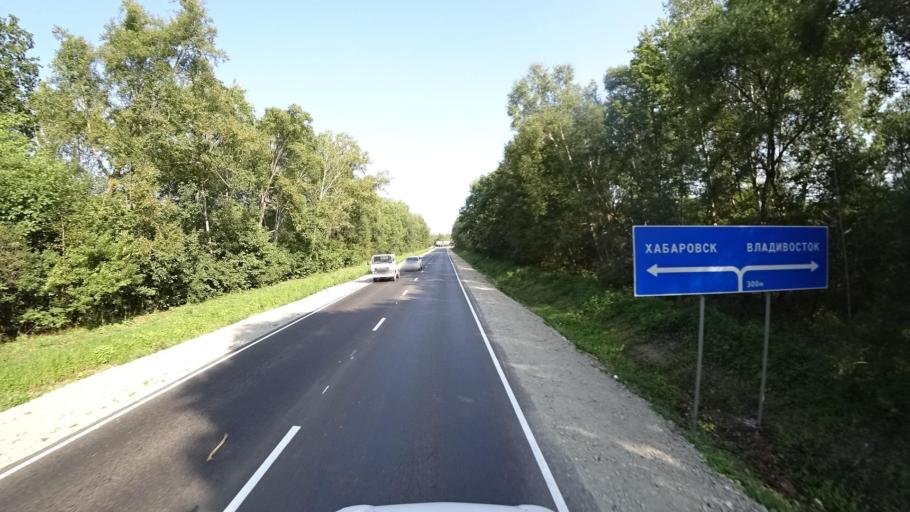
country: RU
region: Khabarovsk Krai
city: Khor
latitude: 47.9759
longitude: 135.0783
